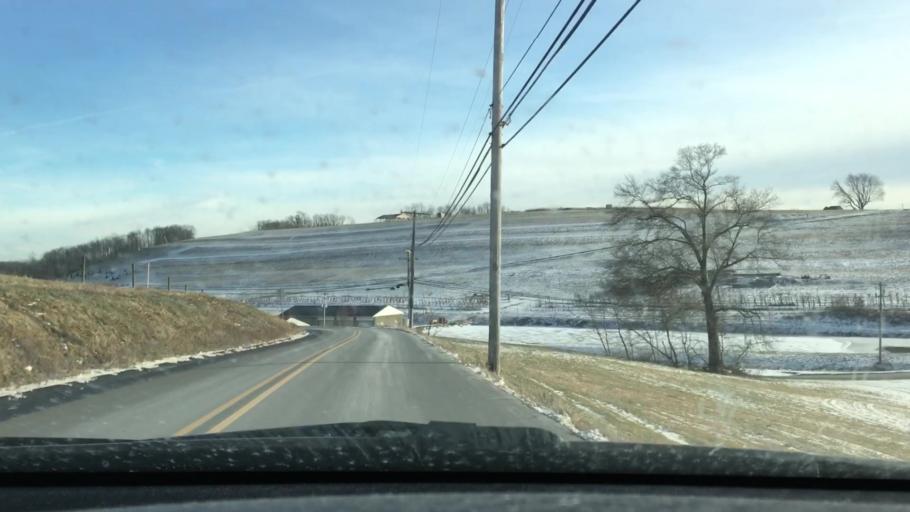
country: US
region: Pennsylvania
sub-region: Washington County
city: Gastonville
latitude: 40.2778
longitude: -80.0339
